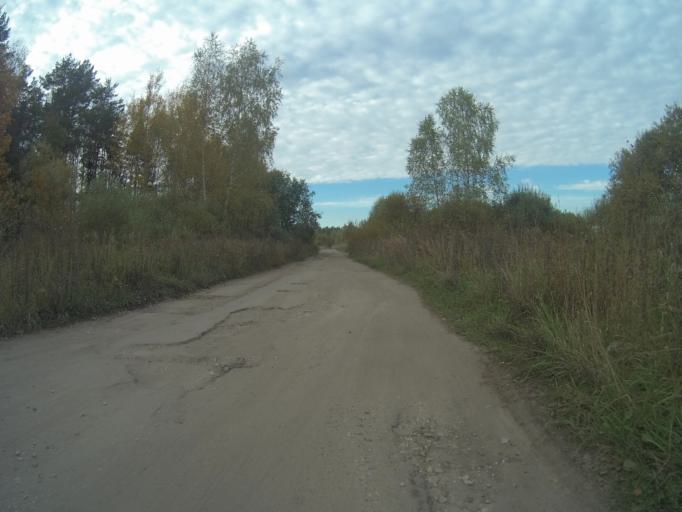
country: RU
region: Vladimir
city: Golovino
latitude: 55.9636
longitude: 40.4225
